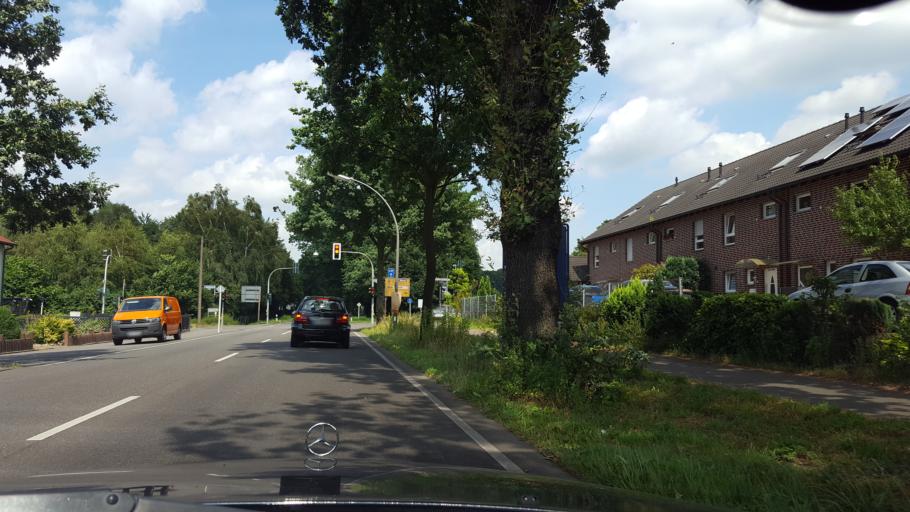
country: DE
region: North Rhine-Westphalia
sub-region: Regierungsbezirk Munster
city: Recklinghausen
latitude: 51.6688
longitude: 7.1791
